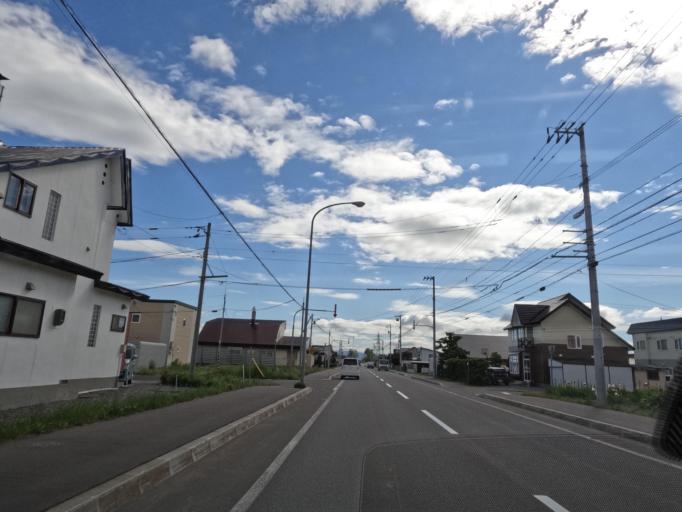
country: JP
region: Hokkaido
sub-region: Asahikawa-shi
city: Asahikawa
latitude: 43.8267
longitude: 142.5231
